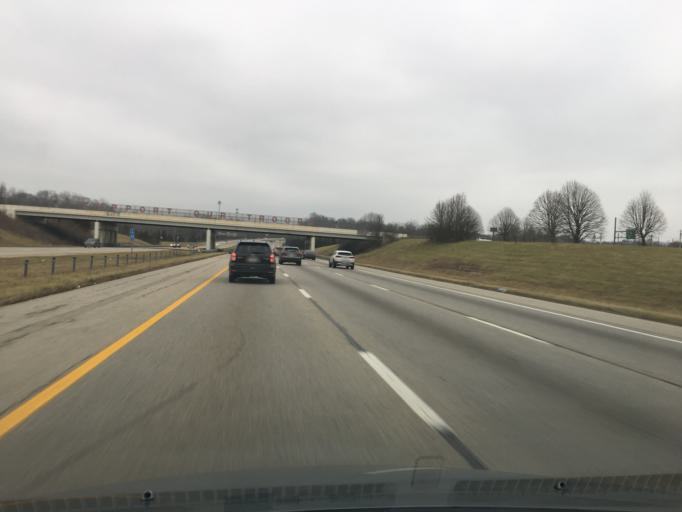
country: US
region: Ohio
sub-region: Hamilton County
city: The Village of Indian Hill
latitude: 39.2267
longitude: -84.2813
